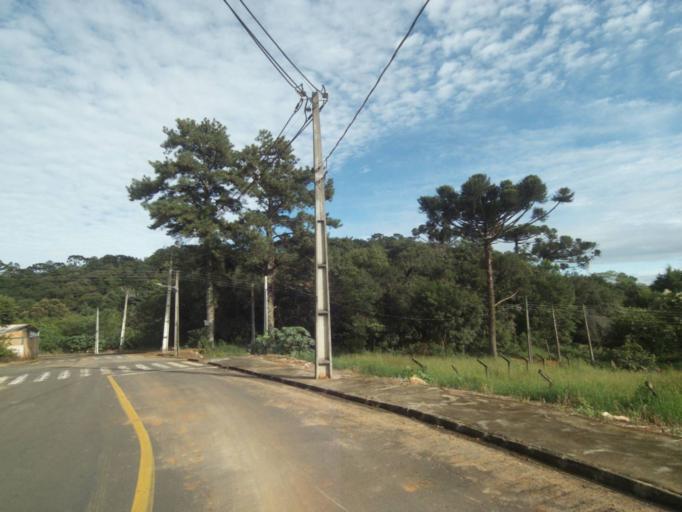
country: BR
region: Parana
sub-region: Telemaco Borba
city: Telemaco Borba
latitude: -24.3425
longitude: -50.6062
